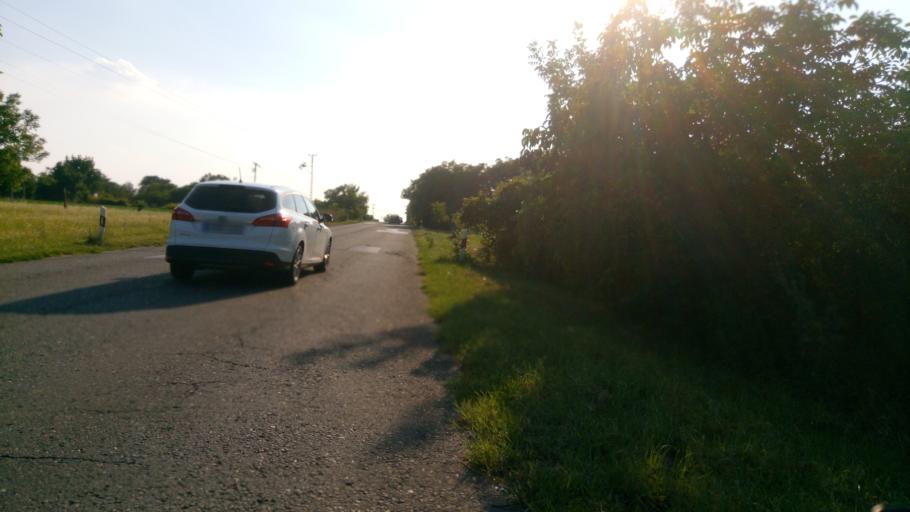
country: HU
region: Pest
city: Budaors
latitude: 47.4462
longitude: 18.9548
